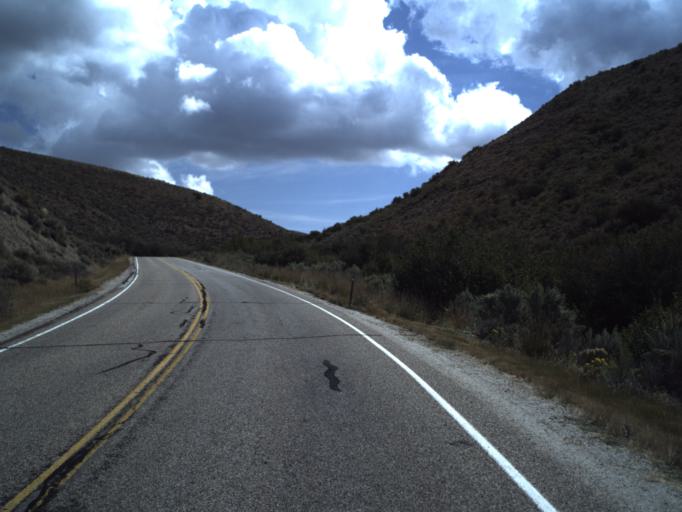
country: US
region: Utah
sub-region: Rich County
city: Randolph
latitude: 41.8187
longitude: -111.2812
